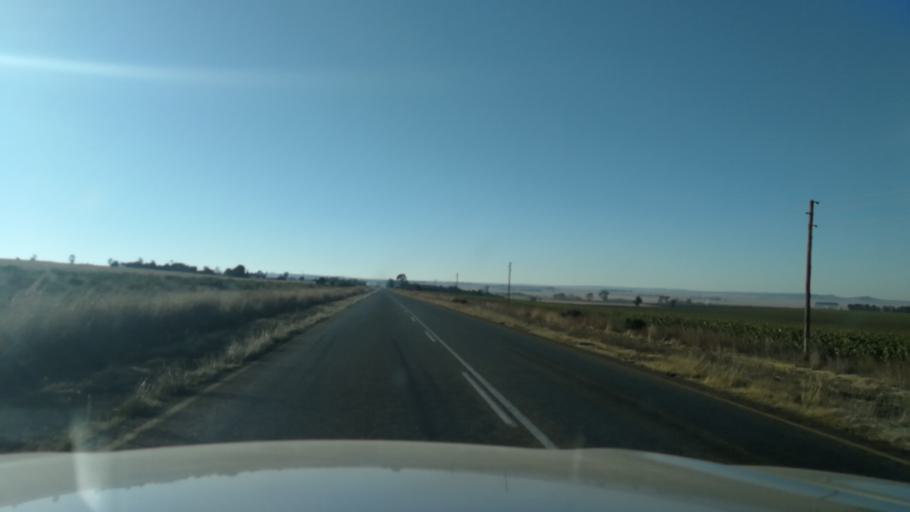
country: ZA
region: North-West
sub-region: Bojanala Platinum District Municipality
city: Koster
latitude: -25.9172
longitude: 27.0748
